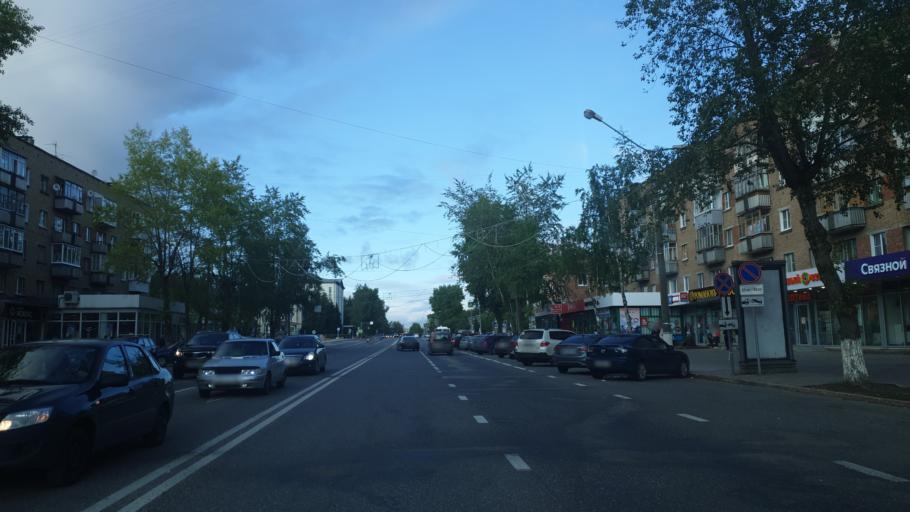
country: RU
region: Komi Republic
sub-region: Syktyvdinskiy Rayon
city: Syktyvkar
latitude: 61.6642
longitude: 50.8175
